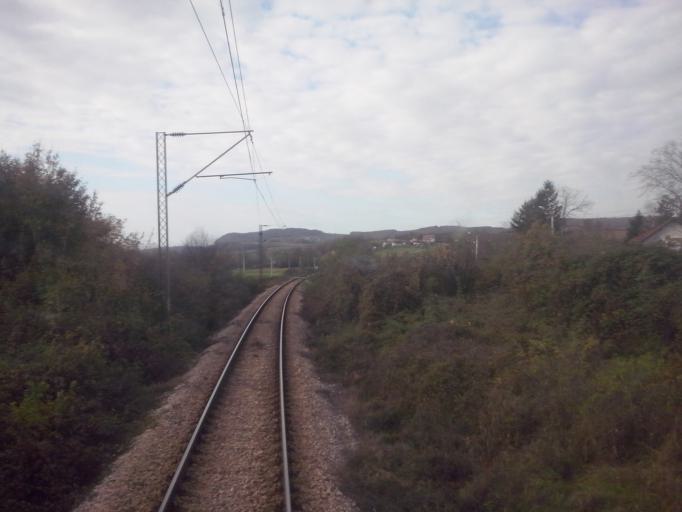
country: RS
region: Central Serbia
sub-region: Kolubarski Okrug
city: Lajkovac
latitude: 44.3549
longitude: 20.1070
